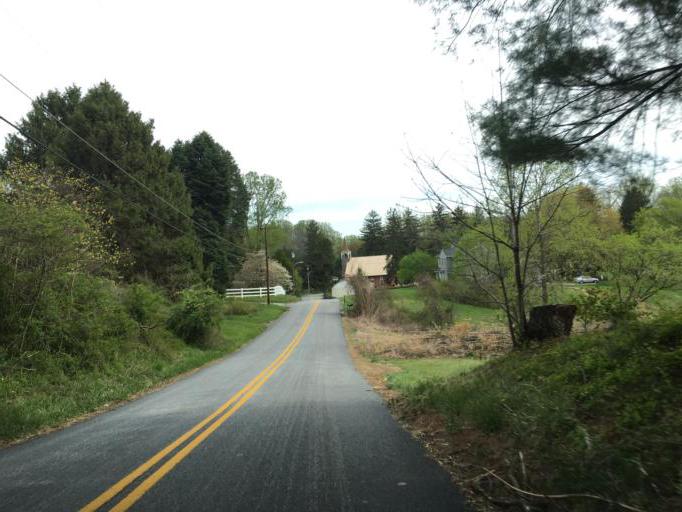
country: US
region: Maryland
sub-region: Baltimore County
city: Hunt Valley
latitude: 39.4989
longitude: -76.6107
